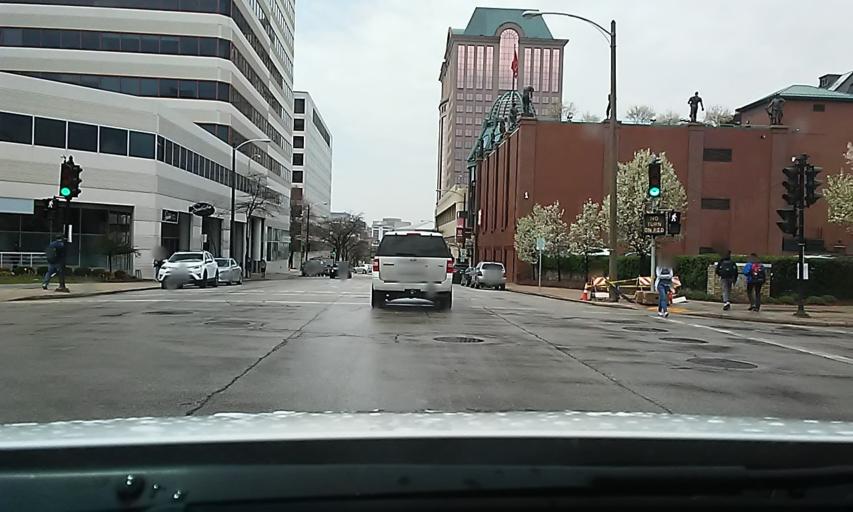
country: US
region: Wisconsin
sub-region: Milwaukee County
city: Milwaukee
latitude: 43.0437
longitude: -87.9069
